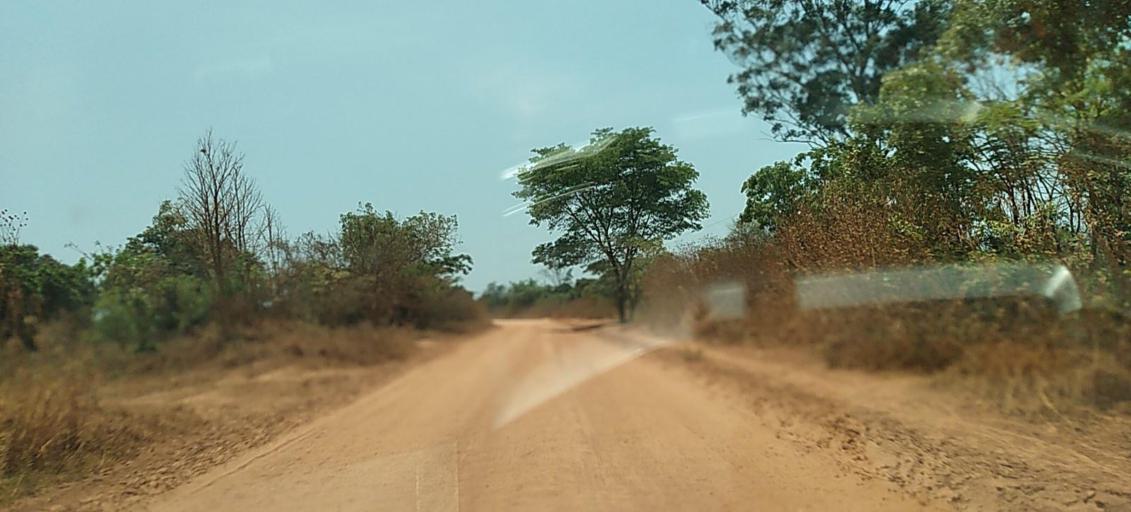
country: CD
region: Katanga
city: Kipushi
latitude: -11.7826
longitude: 27.1800
